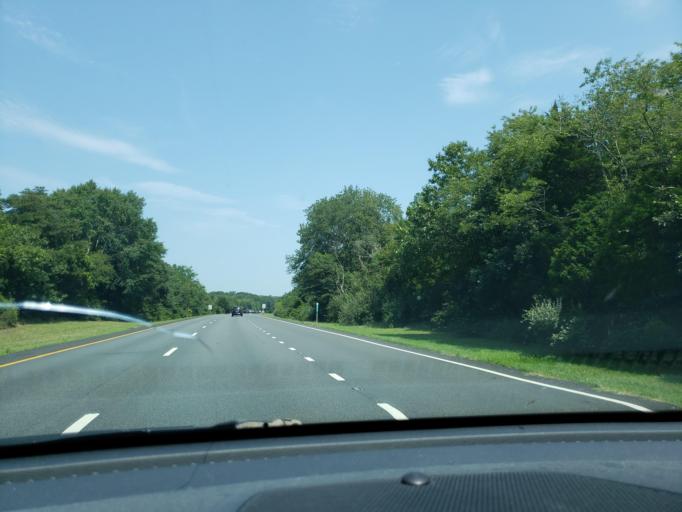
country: US
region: New Jersey
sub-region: Cape May County
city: Ocean City
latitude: 39.2661
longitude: -74.6397
